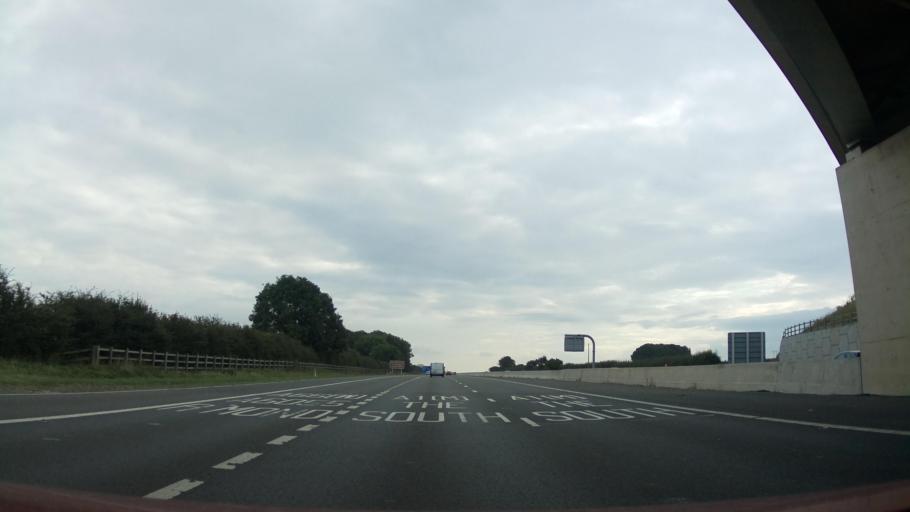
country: GB
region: England
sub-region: Darlington
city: High Coniscliffe
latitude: 54.4519
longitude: -1.6672
